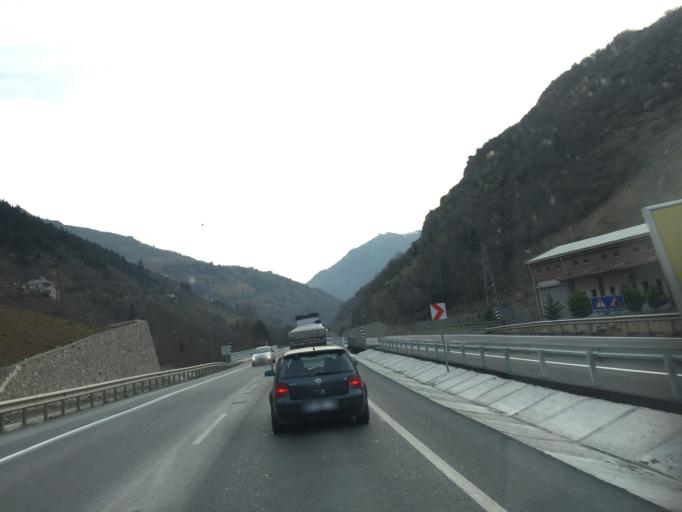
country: TR
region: Trabzon
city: Macka
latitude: 40.7963
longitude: 39.5842
